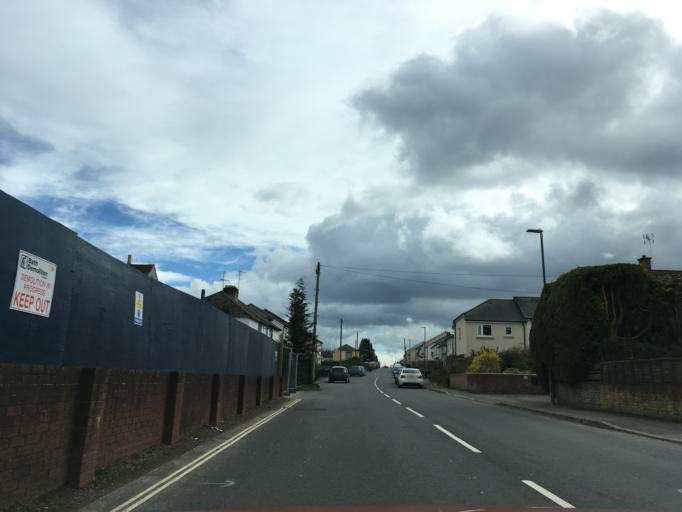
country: GB
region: England
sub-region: Gloucestershire
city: Coleford
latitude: 51.7855
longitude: -2.6116
